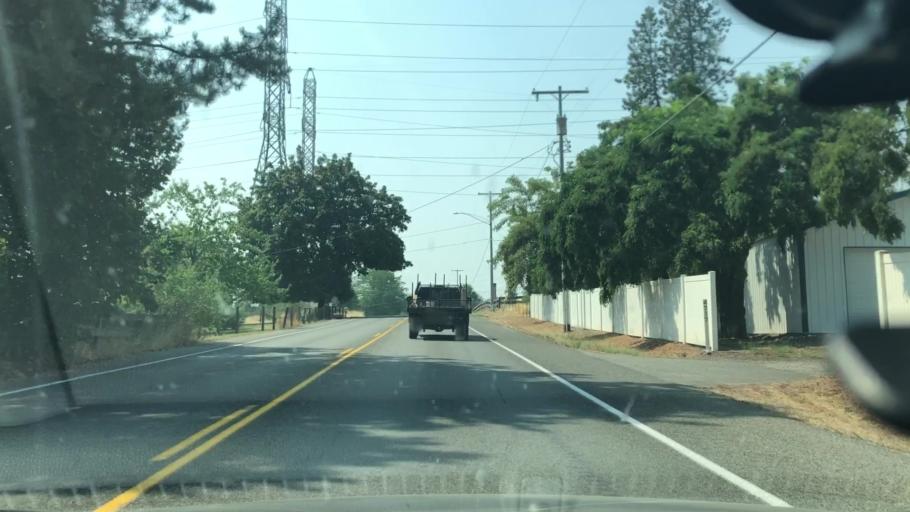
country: US
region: Washington
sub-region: Spokane County
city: Millwood
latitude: 47.6856
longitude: -117.3401
